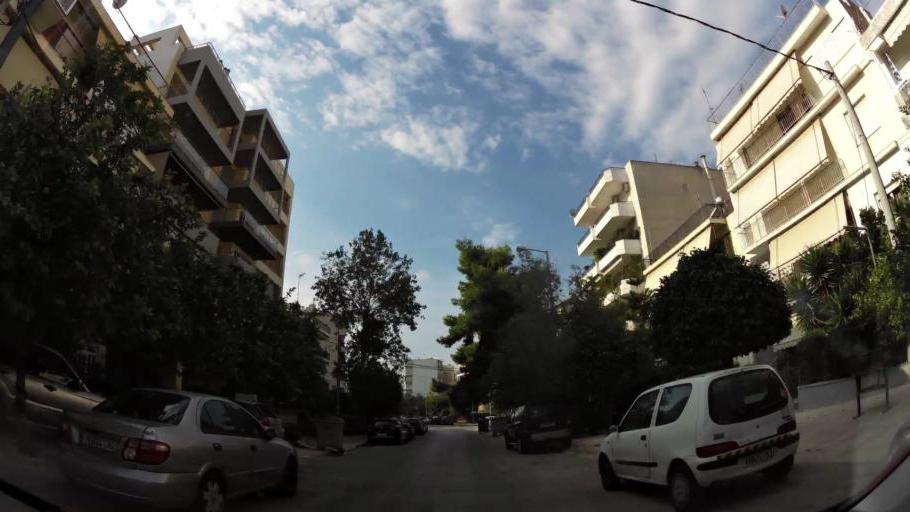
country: GR
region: Attica
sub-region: Nomarchia Athinas
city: Nea Smyrni
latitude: 37.9410
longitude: 23.7086
